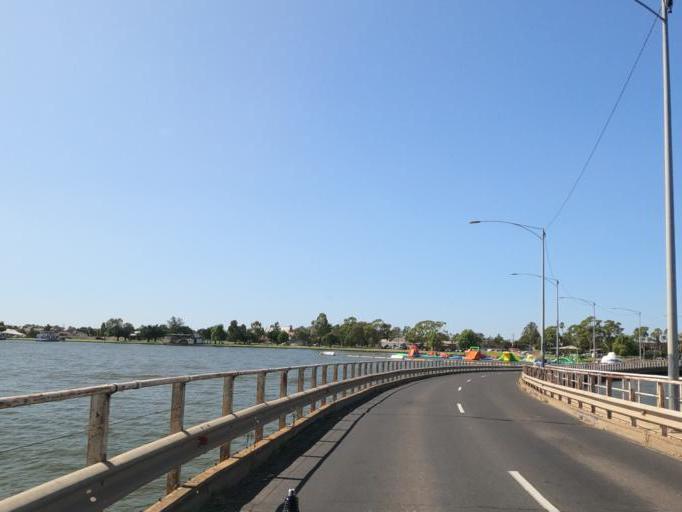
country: AU
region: New South Wales
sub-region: Corowa Shire
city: Mulwala
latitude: -36.0051
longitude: 146.0048
